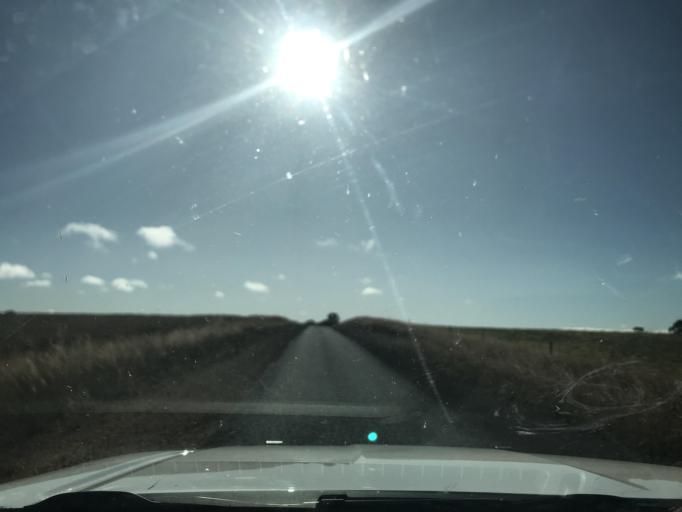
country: AU
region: Victoria
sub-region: Horsham
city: Horsham
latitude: -36.6956
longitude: 141.5803
